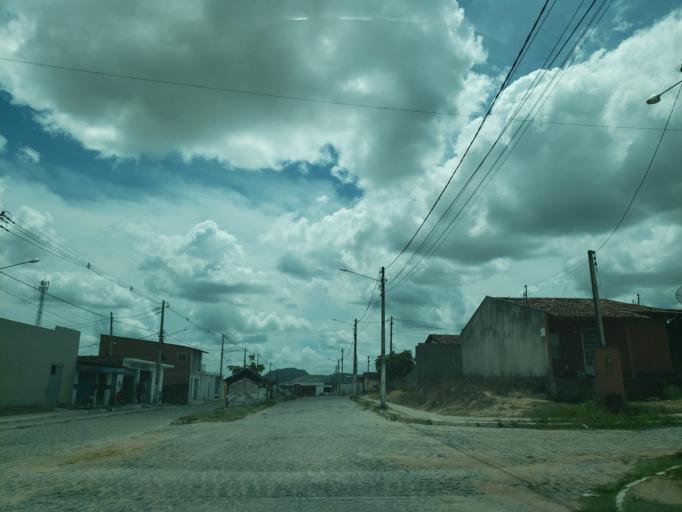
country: BR
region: Alagoas
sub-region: Uniao Dos Palmares
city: Uniao dos Palmares
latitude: -9.1510
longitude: -36.0103
